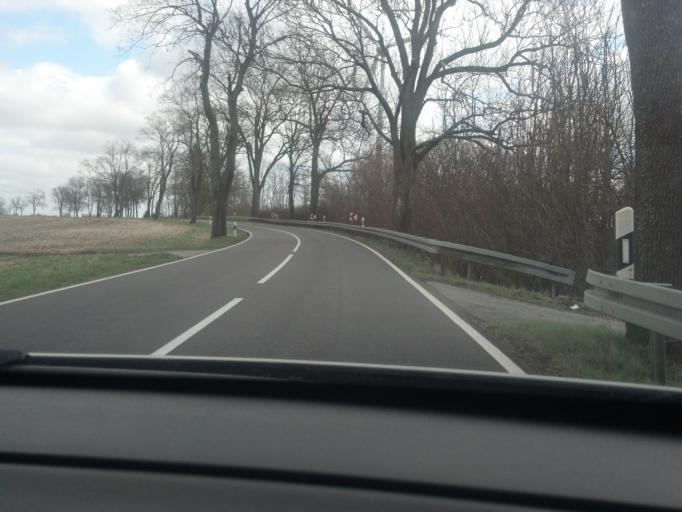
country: DE
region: Brandenburg
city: Gerdshagen
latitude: 53.2984
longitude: 12.2115
